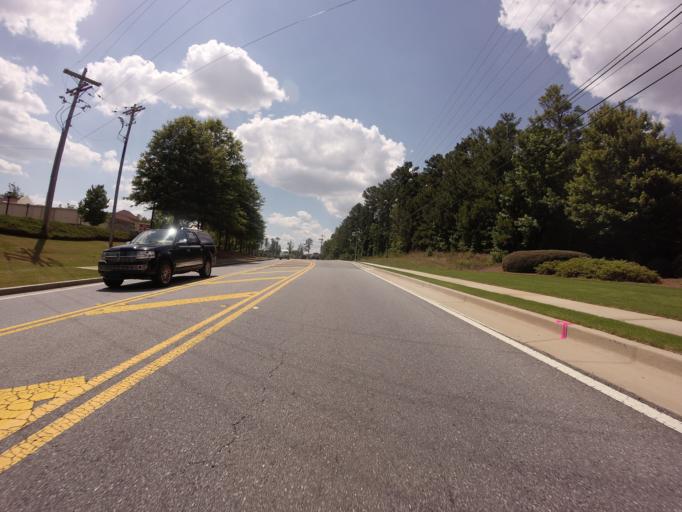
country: US
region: Georgia
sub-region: Fulton County
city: Johns Creek
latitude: 34.0235
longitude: -84.2507
